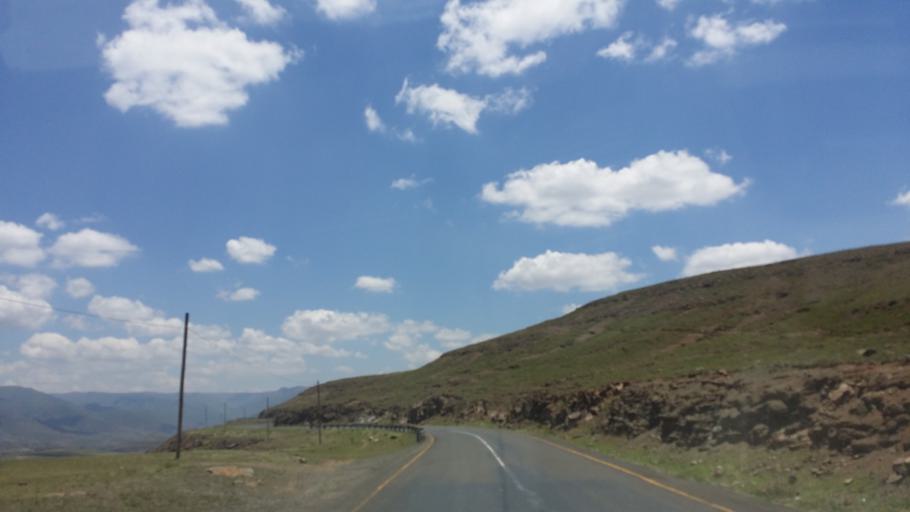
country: LS
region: Mokhotlong
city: Mokhotlong
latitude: -29.2635
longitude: 28.9021
